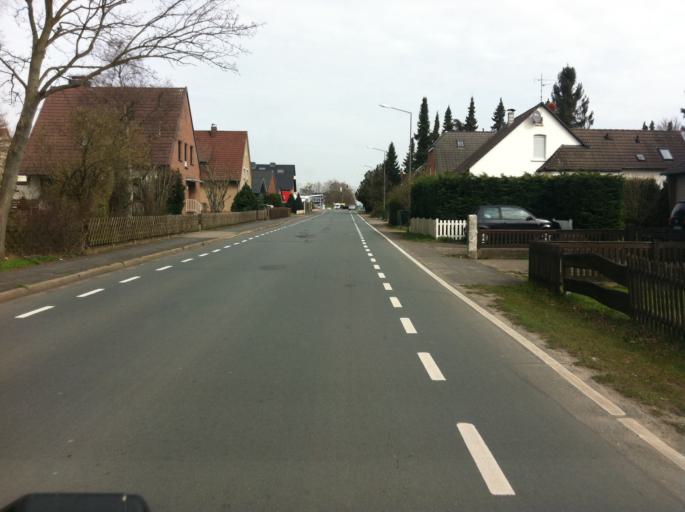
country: DE
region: North Rhine-Westphalia
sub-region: Regierungsbezirk Detmold
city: Minden
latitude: 52.2909
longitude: 8.8795
